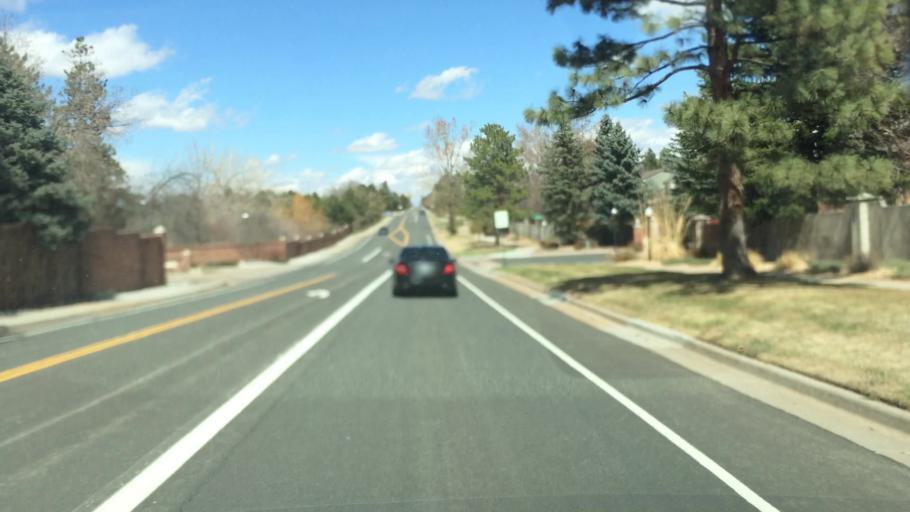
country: US
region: Colorado
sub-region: Arapahoe County
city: Centennial
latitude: 39.6072
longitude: -104.8761
